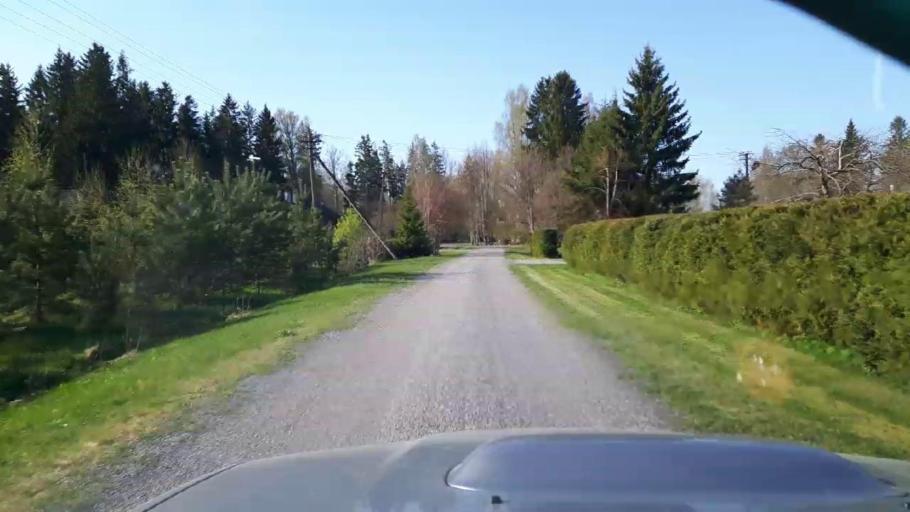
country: EE
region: Paernumaa
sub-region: Tootsi vald
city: Tootsi
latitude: 58.4856
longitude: 24.9060
